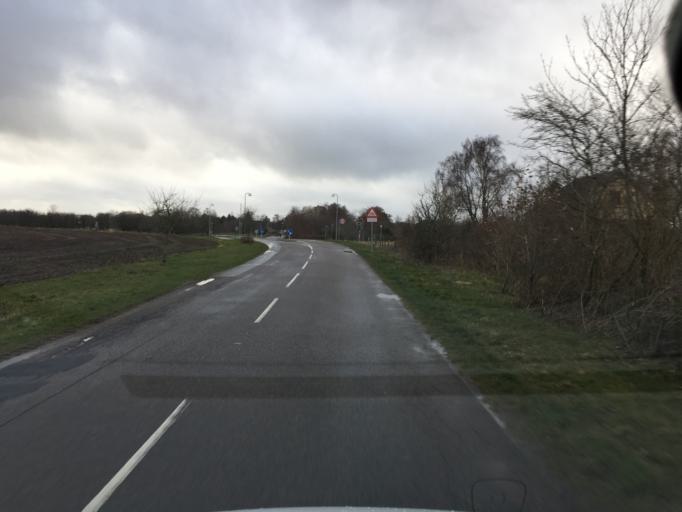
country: DE
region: Schleswig-Holstein
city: Bramstedtlund
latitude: 54.9426
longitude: 9.0987
